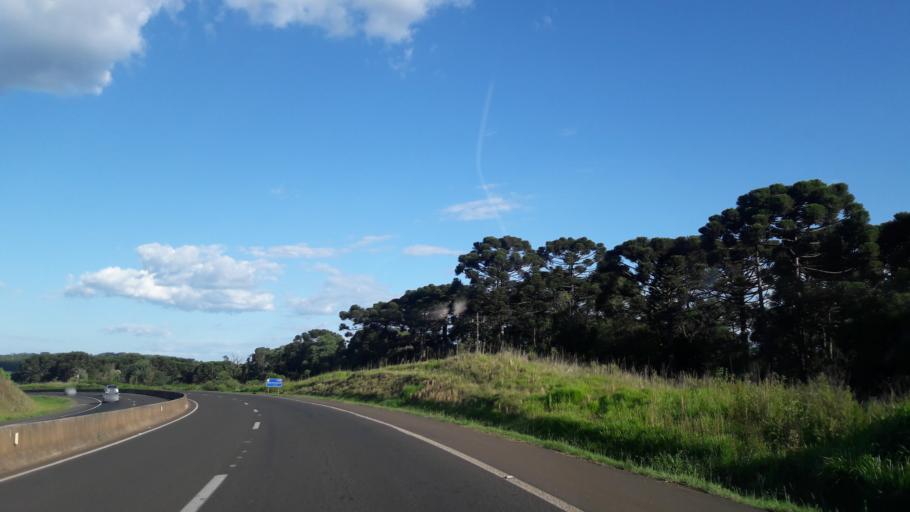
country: BR
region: Parana
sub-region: Guarapuava
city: Guarapuava
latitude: -25.3402
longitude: -51.4247
